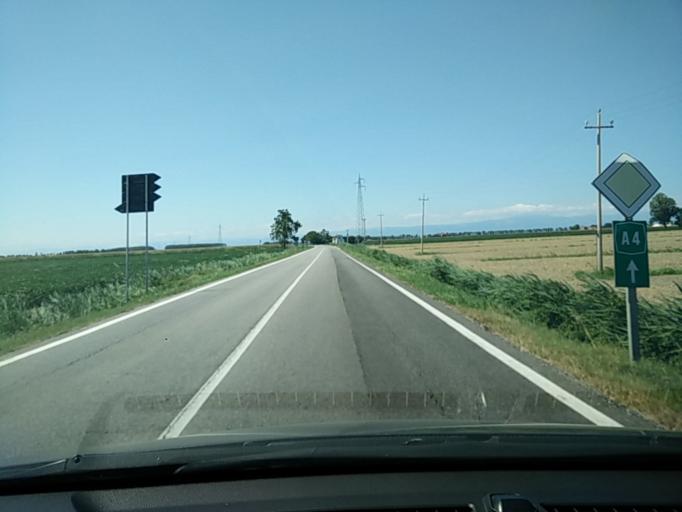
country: IT
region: Veneto
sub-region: Provincia di Venezia
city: La Salute di Livenza
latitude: 45.6554
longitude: 12.8299
